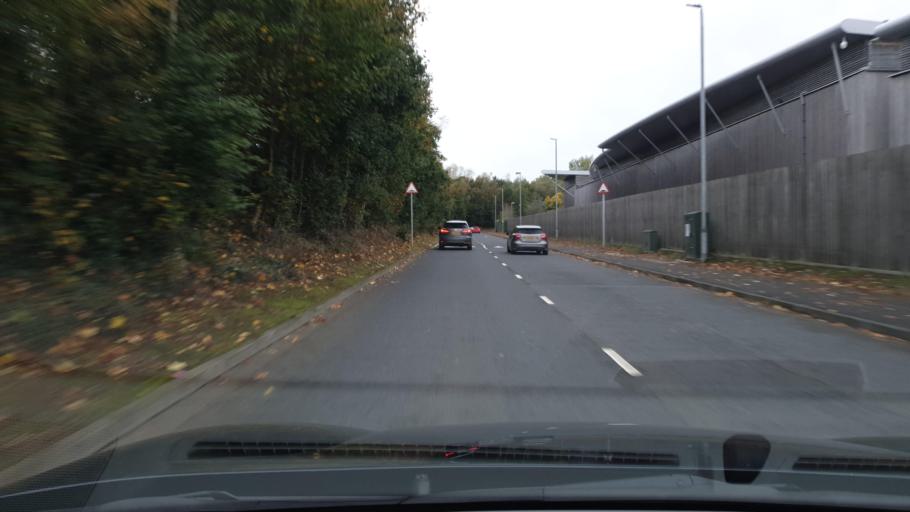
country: GB
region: Northern Ireland
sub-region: Banbridge District
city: Banbridge
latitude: 54.3309
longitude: -6.2739
